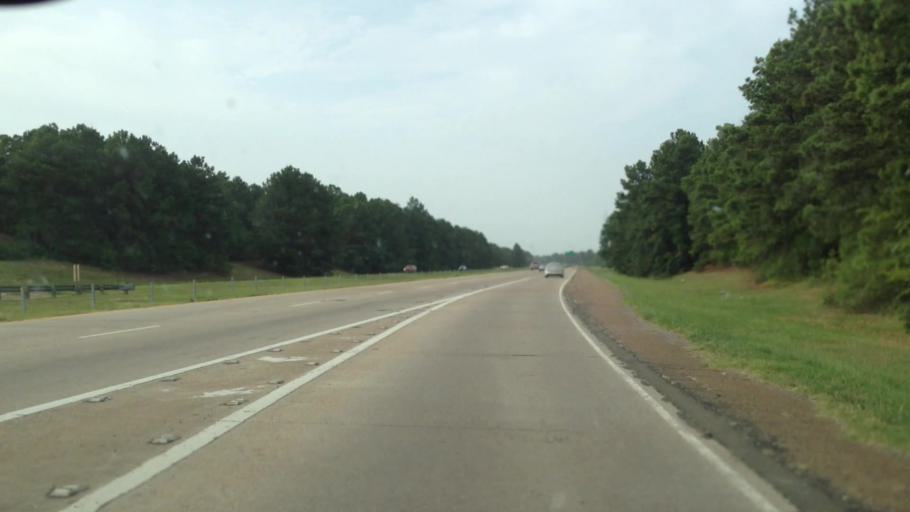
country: US
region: Louisiana
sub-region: Caddo Parish
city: Shreveport
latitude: 32.4393
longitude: -93.8418
